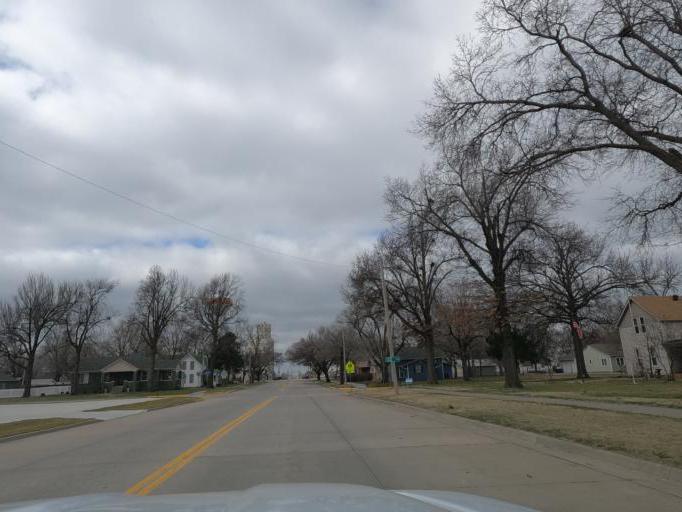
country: US
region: Kansas
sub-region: McPherson County
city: Inman
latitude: 38.2320
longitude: -97.7727
